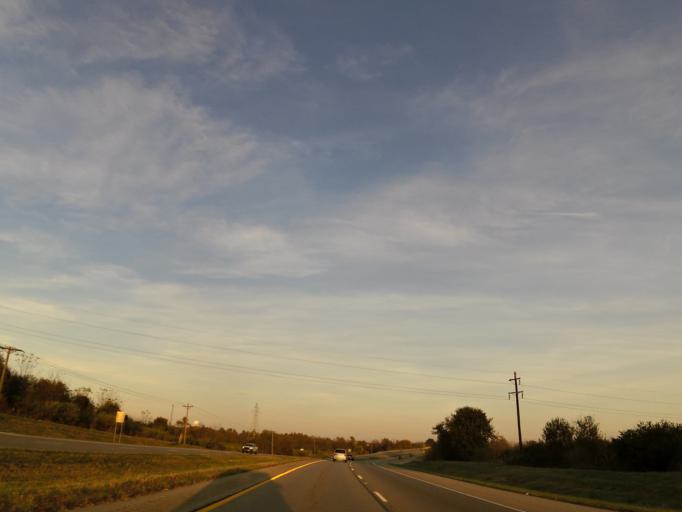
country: US
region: Kentucky
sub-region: Jessamine County
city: Nicholasville
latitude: 37.9034
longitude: -84.5759
